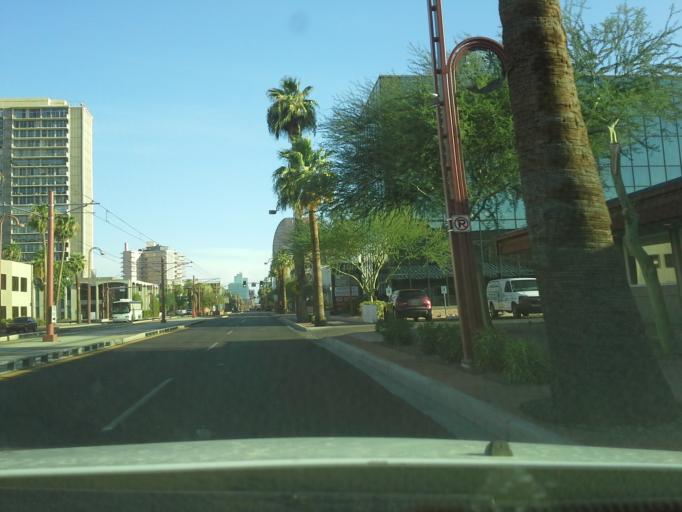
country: US
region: Arizona
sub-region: Maricopa County
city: Phoenix
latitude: 33.4757
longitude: -112.0738
